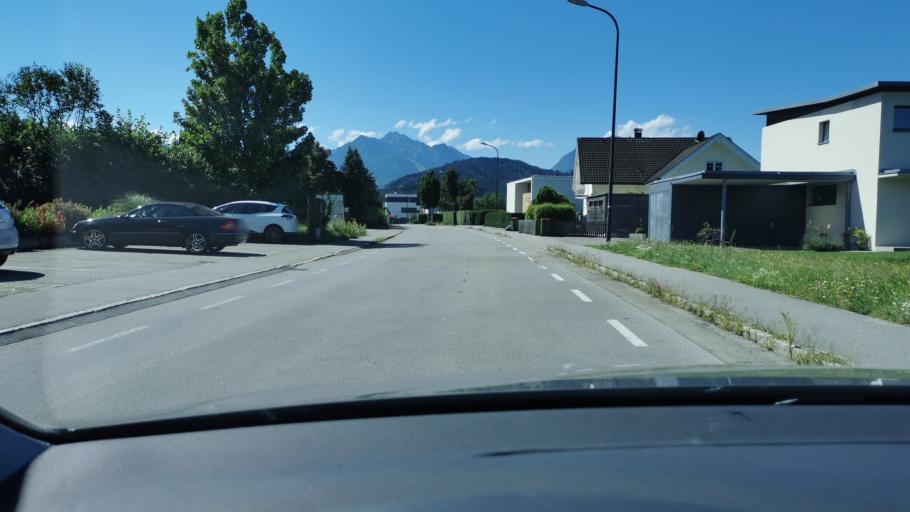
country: AT
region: Vorarlberg
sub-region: Politischer Bezirk Feldkirch
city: Rankweil
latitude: 47.2796
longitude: 9.6451
